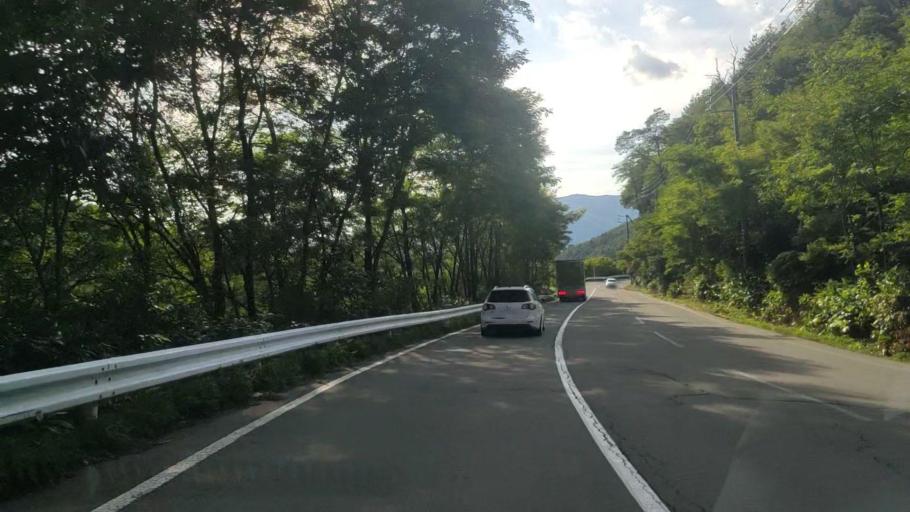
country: JP
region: Nagano
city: Ueda
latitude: 36.4930
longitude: 138.3901
